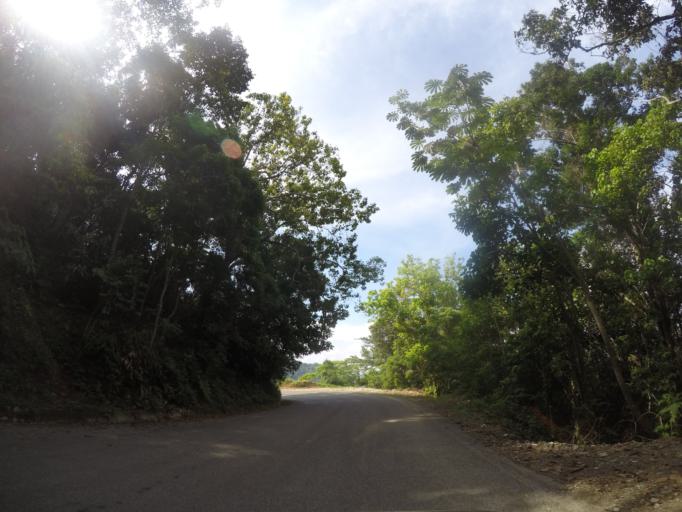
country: MX
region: Oaxaca
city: Pluma Hidalgo
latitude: 15.9378
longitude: -96.4369
